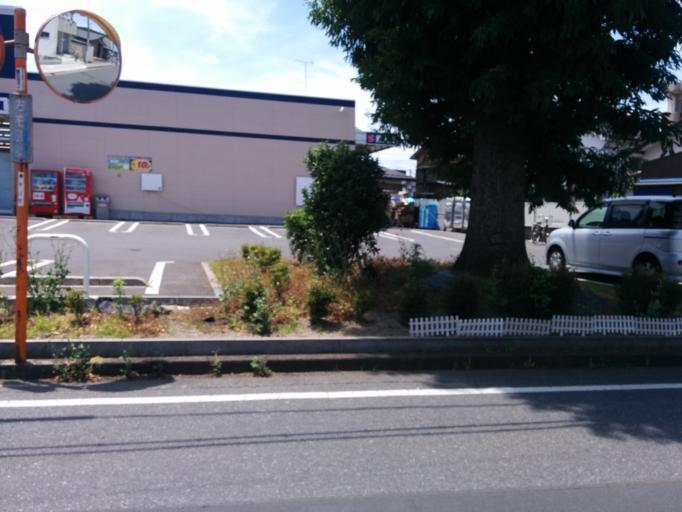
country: JP
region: Tokyo
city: Higashimurayama-shi
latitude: 35.7696
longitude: 139.4692
